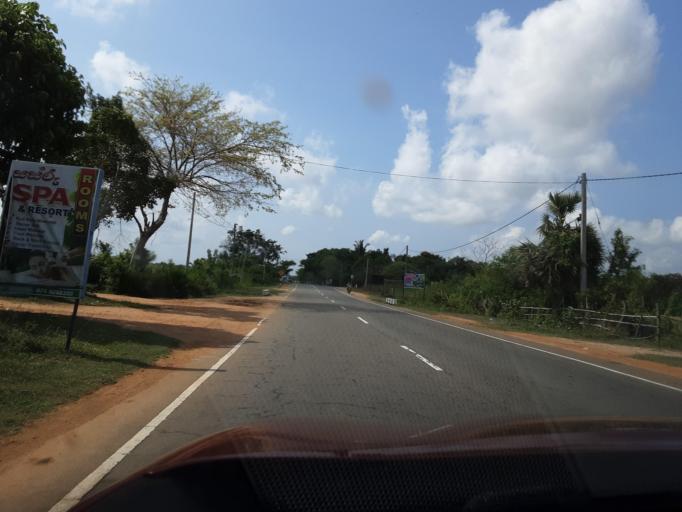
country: LK
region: Southern
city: Tangalla
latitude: 6.2364
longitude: 81.2275
